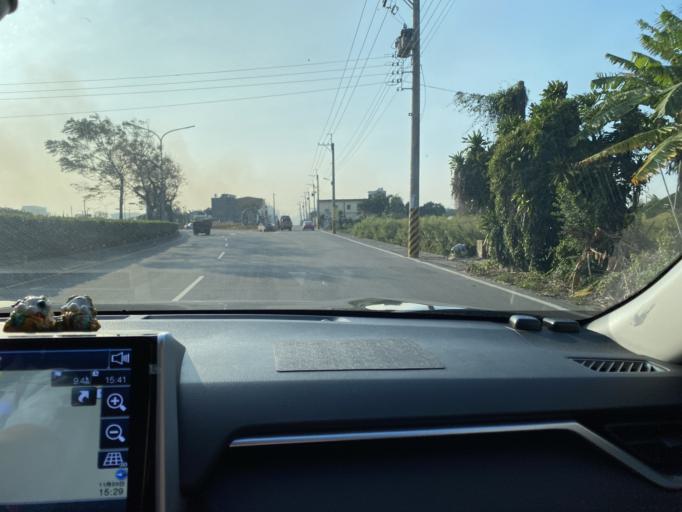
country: TW
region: Taiwan
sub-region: Changhua
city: Chang-hua
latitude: 23.9545
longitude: 120.4285
